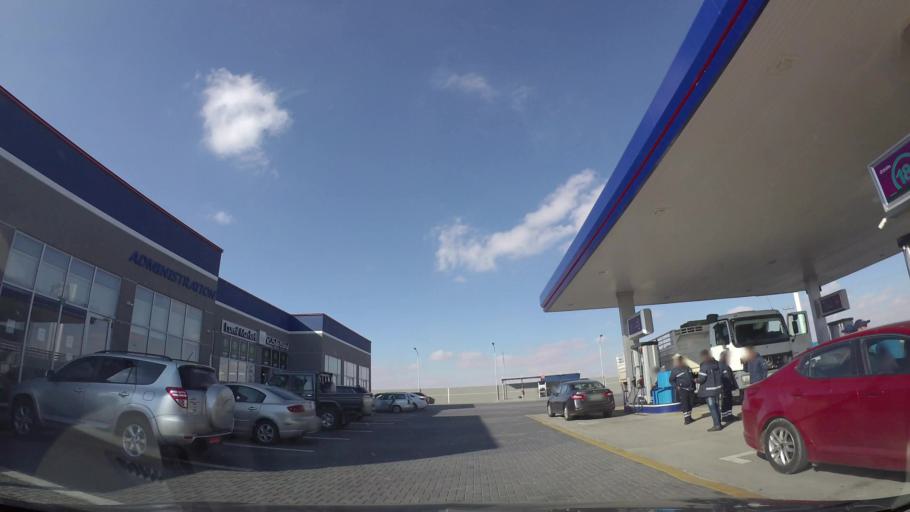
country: JO
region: Karak
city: Adir
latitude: 31.2800
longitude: 36.0540
